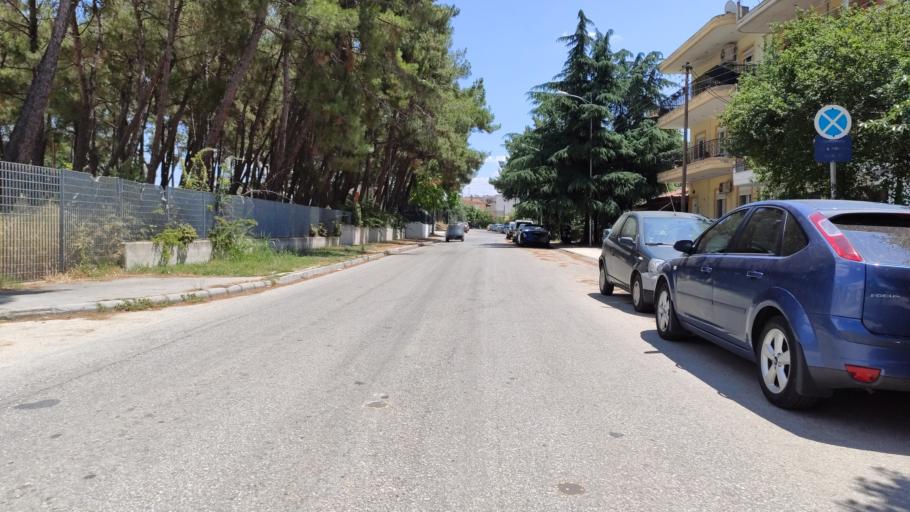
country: GR
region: East Macedonia and Thrace
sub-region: Nomos Rodopis
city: Komotini
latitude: 41.1283
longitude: 25.4110
